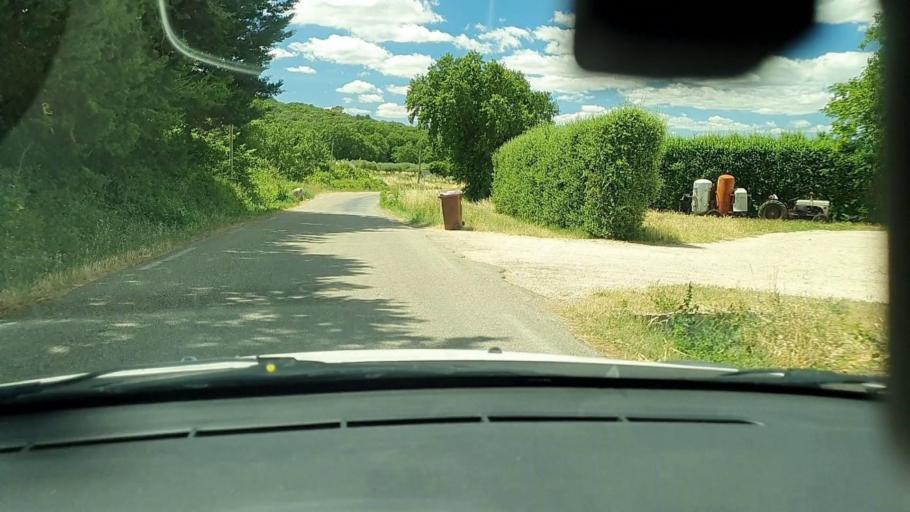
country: FR
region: Languedoc-Roussillon
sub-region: Departement du Gard
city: Poulx
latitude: 43.9516
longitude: 4.4222
